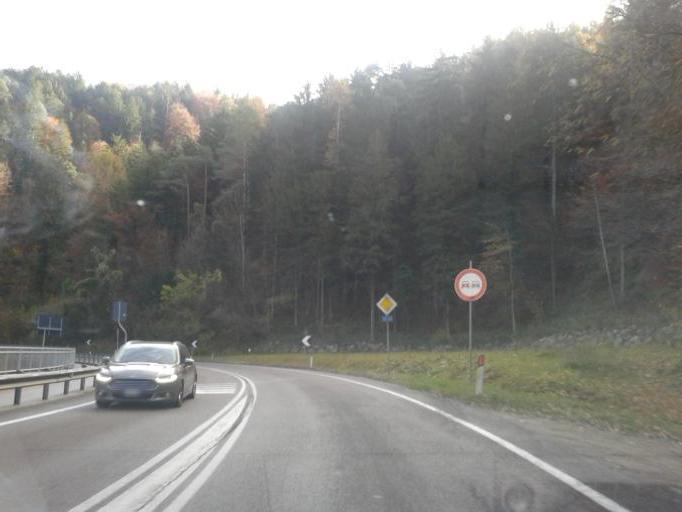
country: IT
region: Trentino-Alto Adige
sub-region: Provincia di Trento
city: Ponte Arche
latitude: 46.0455
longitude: 10.8940
